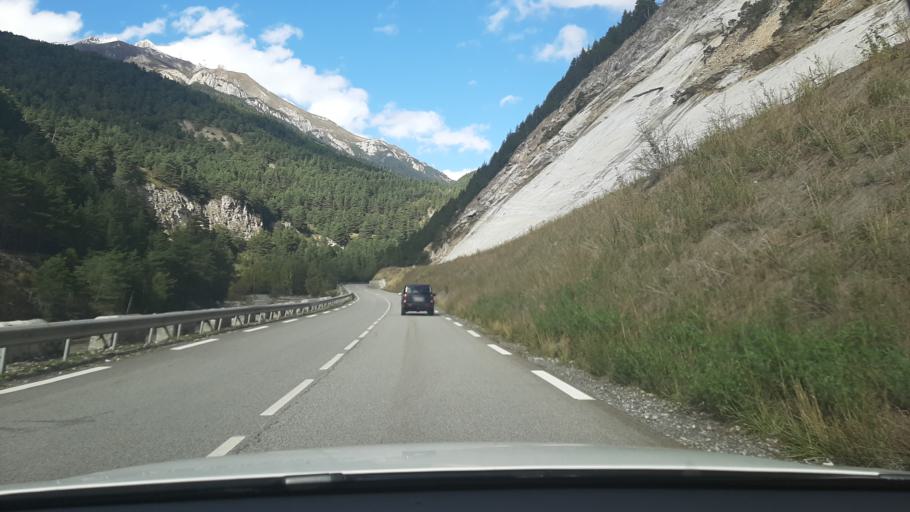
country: FR
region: Rhone-Alpes
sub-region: Departement de la Savoie
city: Modane
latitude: 45.2205
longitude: 6.7617
